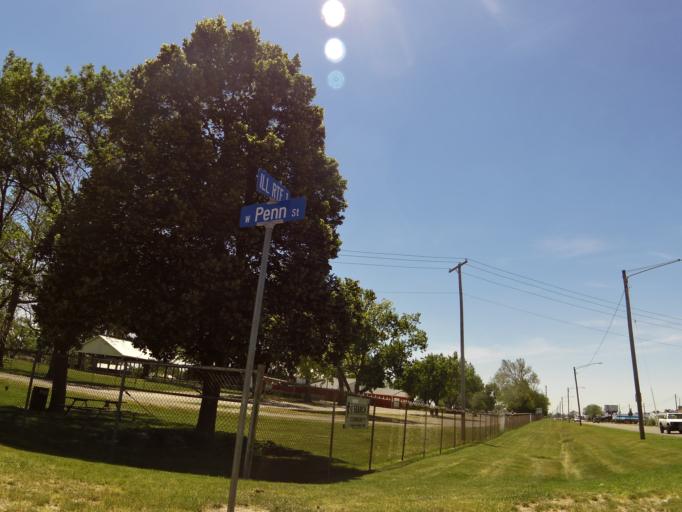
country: US
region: Illinois
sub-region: Vermilion County
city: Hoopeston
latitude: 40.4659
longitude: -87.6875
